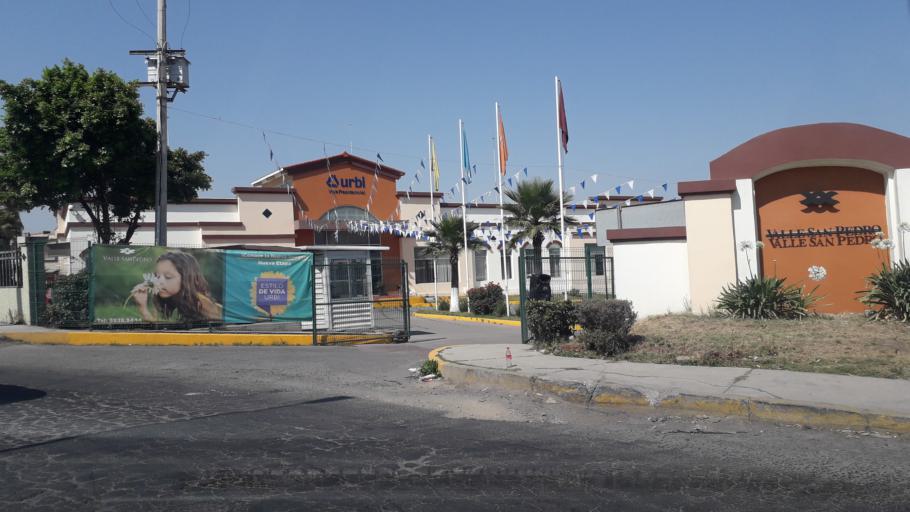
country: MX
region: Mexico
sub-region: Tecamac
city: Ojo de Agua
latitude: 19.6636
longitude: -99.0112
